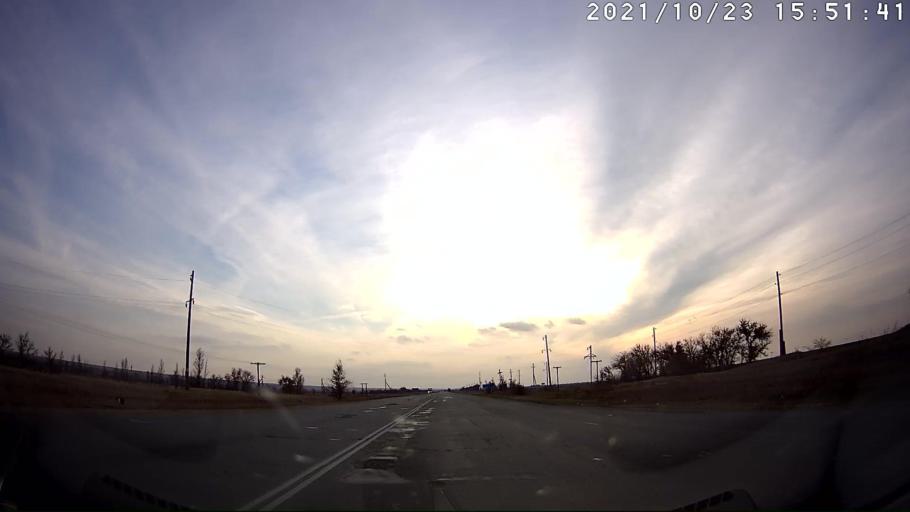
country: RU
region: Kalmykiya
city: Sadovoye
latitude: 47.9941
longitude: 44.0291
